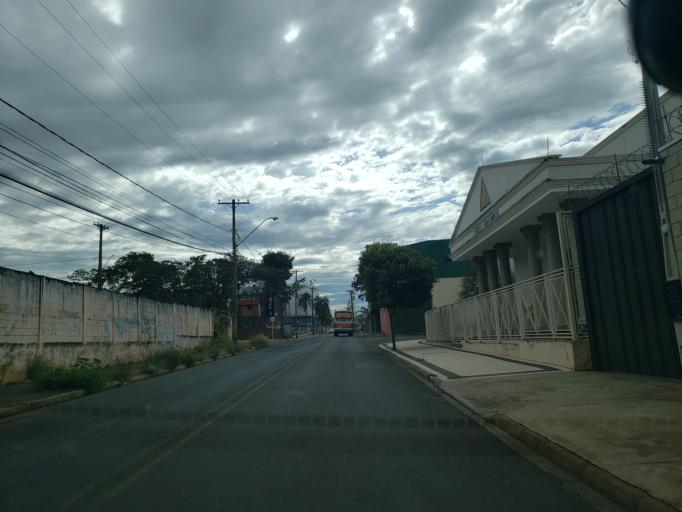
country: BR
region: Sao Paulo
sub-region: Bauru
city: Bauru
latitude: -22.3411
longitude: -49.0441
